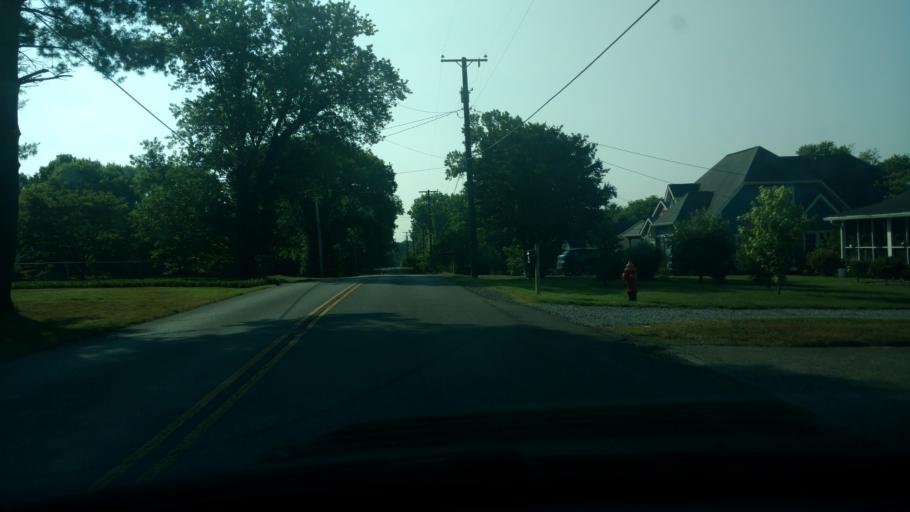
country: US
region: Tennessee
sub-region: Davidson County
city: Nashville
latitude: 36.2207
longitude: -86.7201
